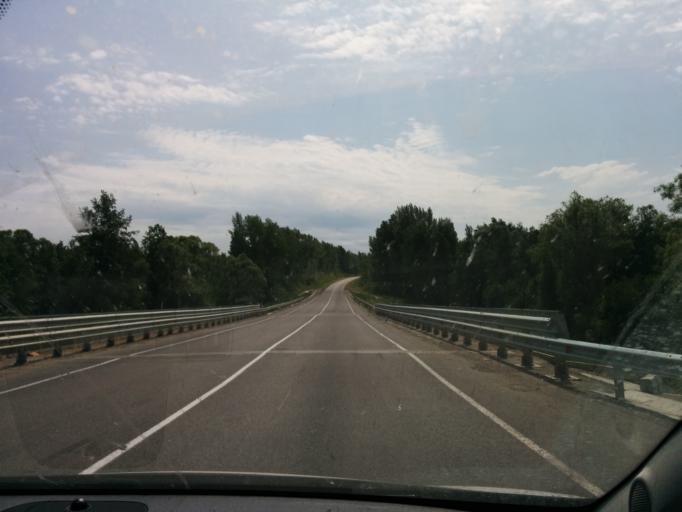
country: RU
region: Tambov
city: Morshansk
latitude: 53.5397
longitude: 41.7909
